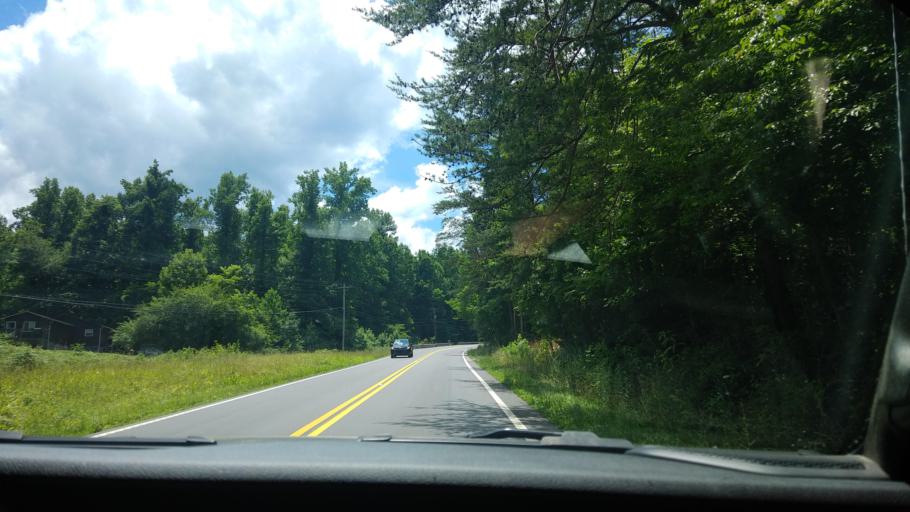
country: US
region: Tennessee
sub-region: Cocke County
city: Newport
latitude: 35.7775
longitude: -83.2462
